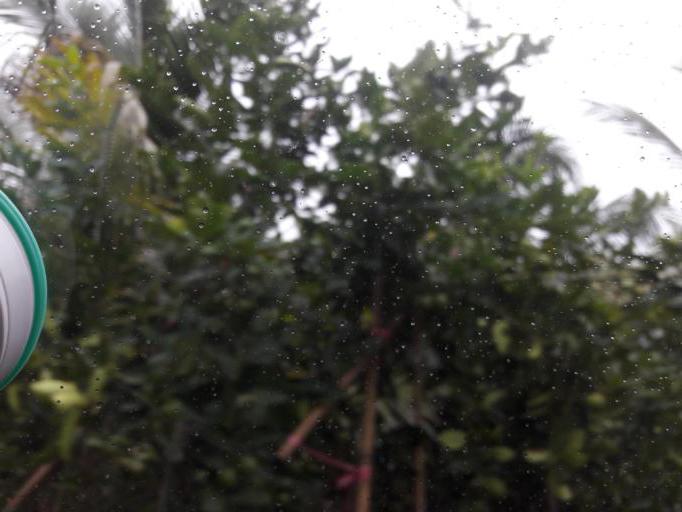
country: TH
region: Ratchaburi
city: Damnoen Saduak
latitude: 13.5116
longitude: 100.0149
